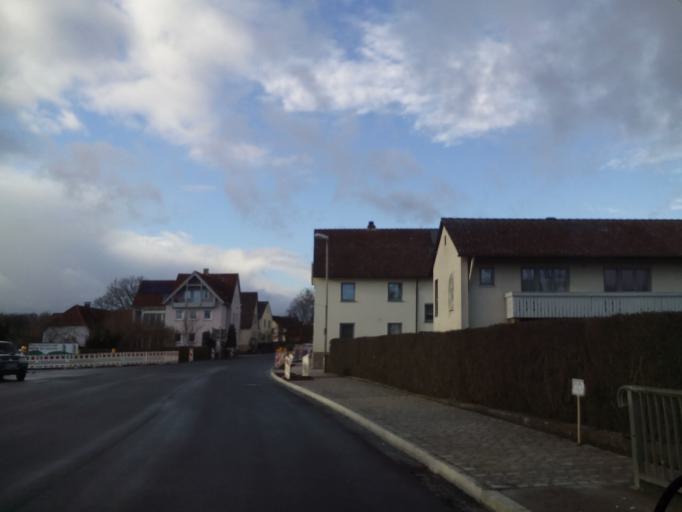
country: DE
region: Bavaria
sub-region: Regierungsbezirk Unterfranken
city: Gossenheim
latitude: 50.0161
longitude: 9.7847
